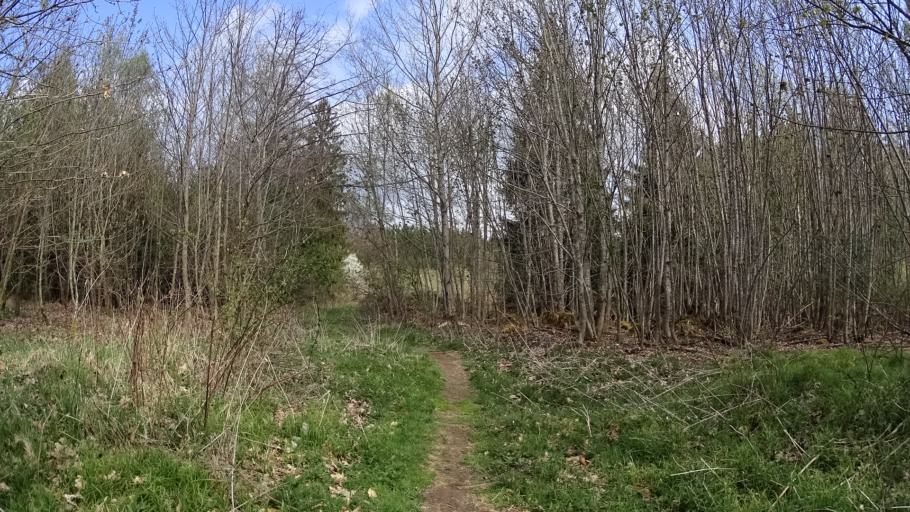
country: DE
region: Bavaria
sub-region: Upper Bavaria
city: Wettstetten
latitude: 48.8546
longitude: 11.4039
